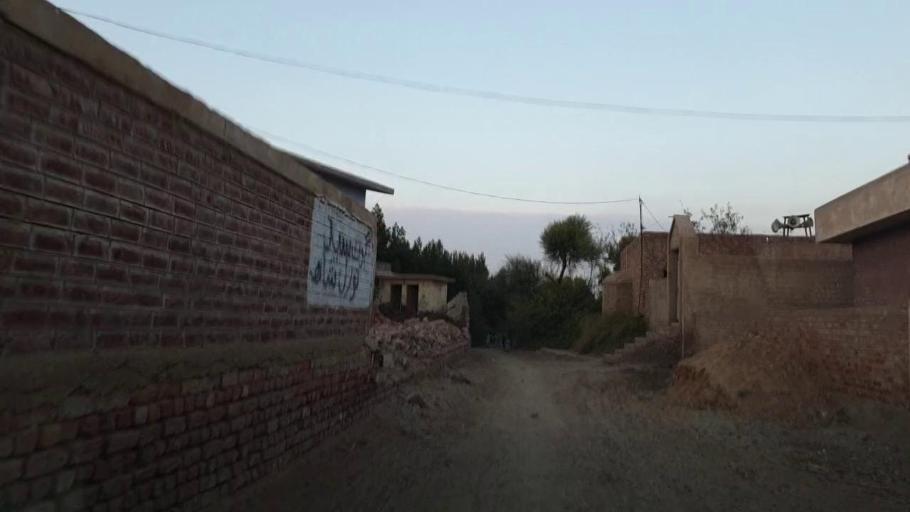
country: PK
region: Sindh
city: Tando Jam
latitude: 25.5053
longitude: 68.5847
